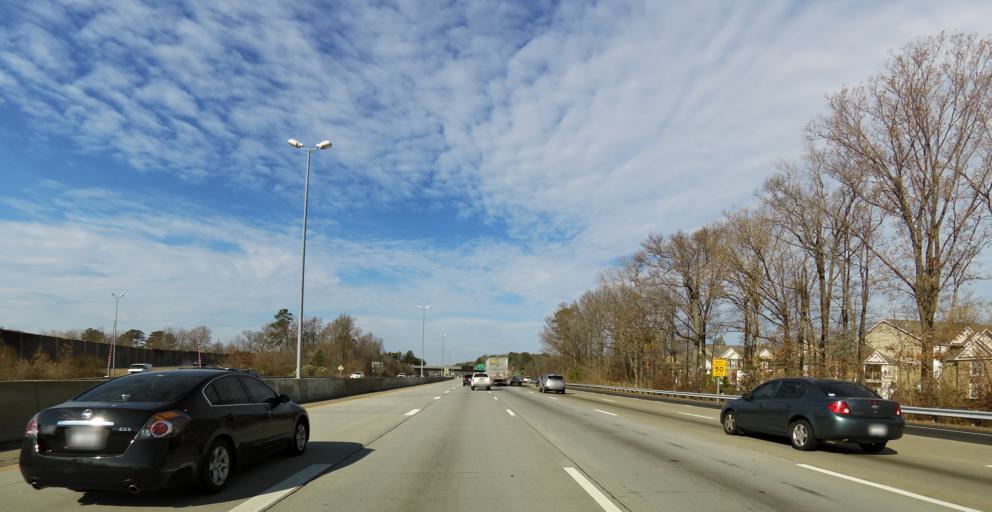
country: US
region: Virginia
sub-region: City of Hampton
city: Hampton
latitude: 37.0486
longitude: -76.4033
